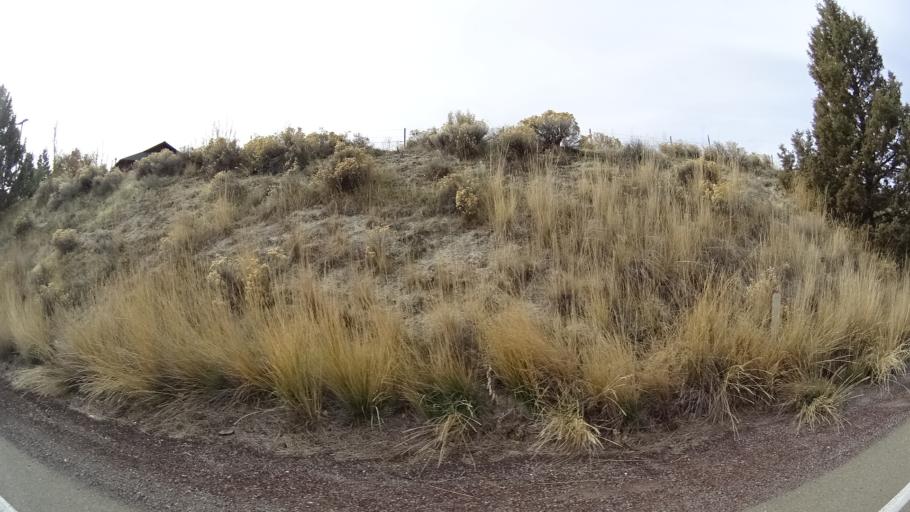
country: US
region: California
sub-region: Siskiyou County
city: Montague
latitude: 41.7005
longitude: -122.5380
